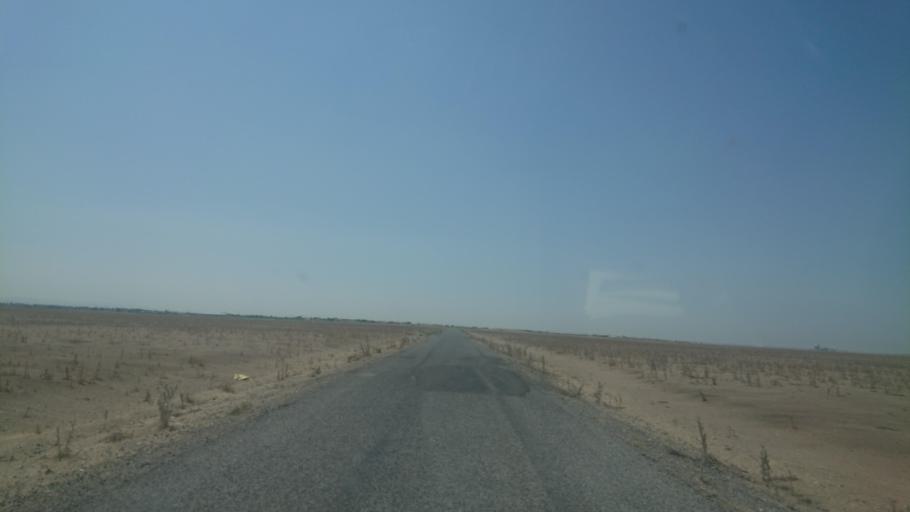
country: TR
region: Aksaray
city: Yesilova
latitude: 38.3085
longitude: 33.7359
